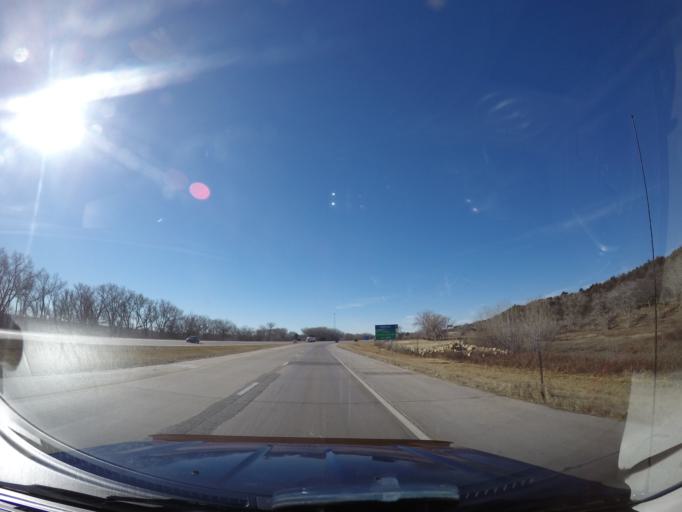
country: US
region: Kansas
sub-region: Geary County
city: Junction City
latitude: 39.0009
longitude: -96.8489
